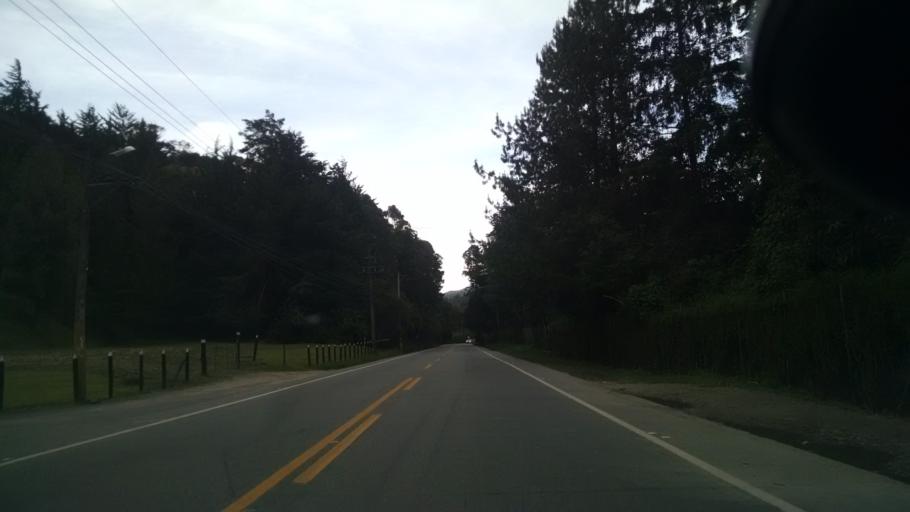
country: CO
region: Antioquia
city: El Retiro
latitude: 6.1018
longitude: -75.5047
